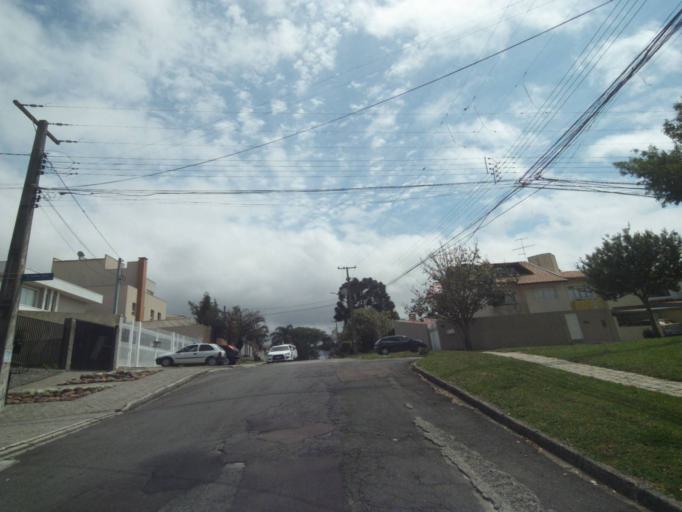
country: BR
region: Parana
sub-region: Pinhais
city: Pinhais
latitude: -25.4340
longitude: -49.2261
